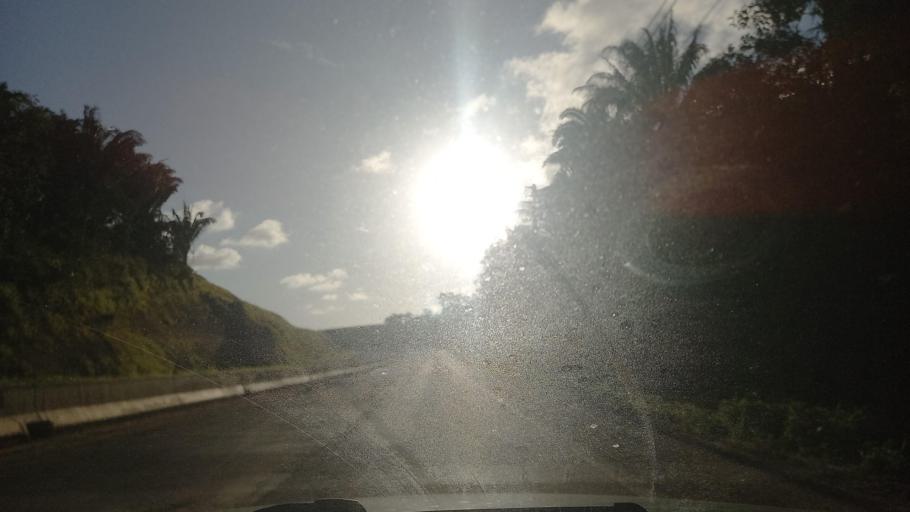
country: BR
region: Alagoas
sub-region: Campo Alegre
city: Campo Alegre
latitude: -9.8223
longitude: -36.2260
